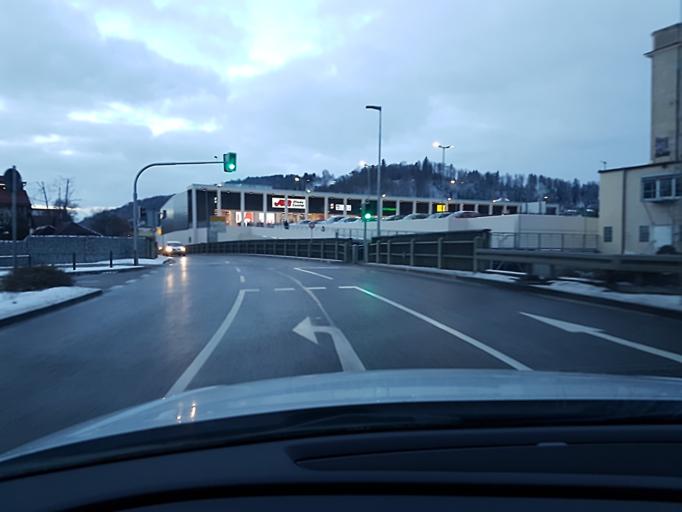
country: DE
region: Baden-Wuerttemberg
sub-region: Regierungsbezirk Stuttgart
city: Murrhardt
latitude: 48.9799
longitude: 9.5817
